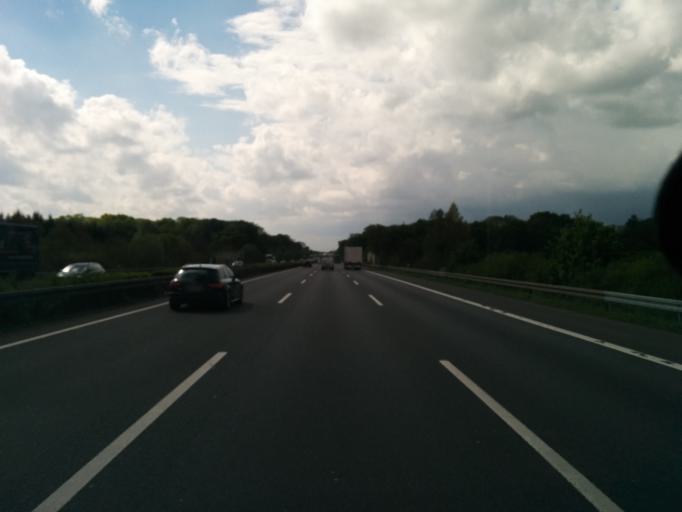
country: DE
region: Lower Saxony
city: Lehre
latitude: 52.3087
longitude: 10.6877
